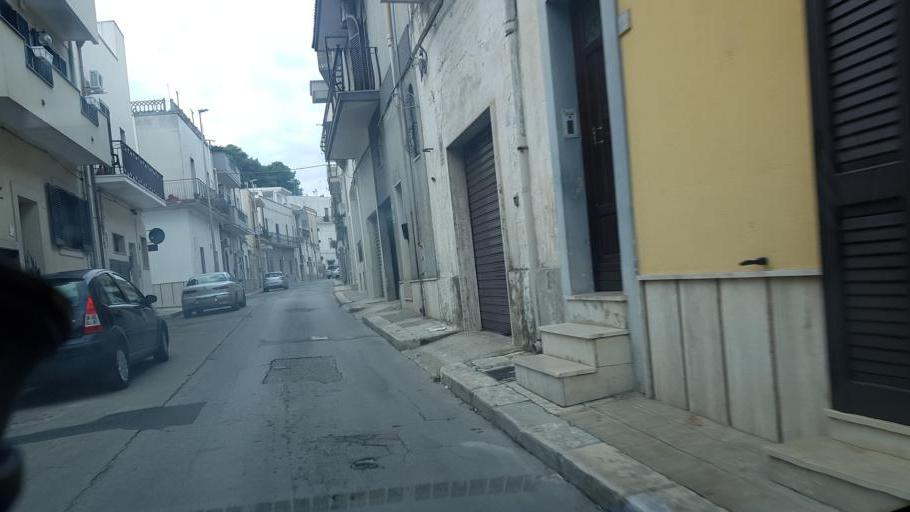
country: IT
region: Apulia
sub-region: Provincia di Brindisi
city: Oria
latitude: 40.4968
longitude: 17.6466
